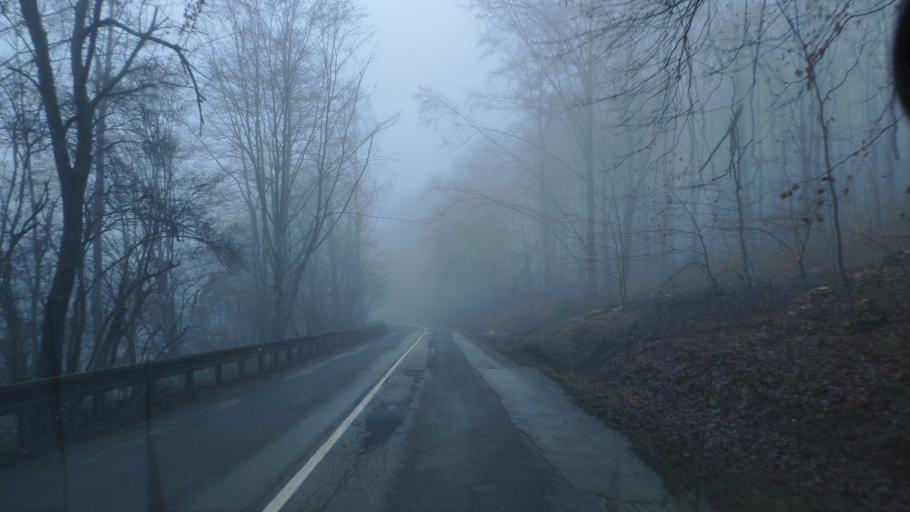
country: SK
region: Kosicky
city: Dobsina
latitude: 48.6385
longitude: 20.3081
